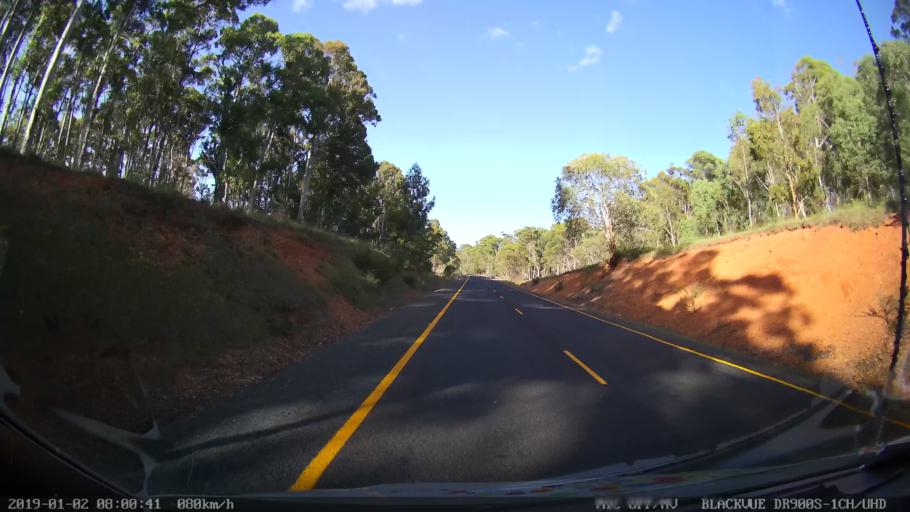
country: AU
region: New South Wales
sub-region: Tumut Shire
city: Tumut
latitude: -35.6454
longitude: 148.4418
